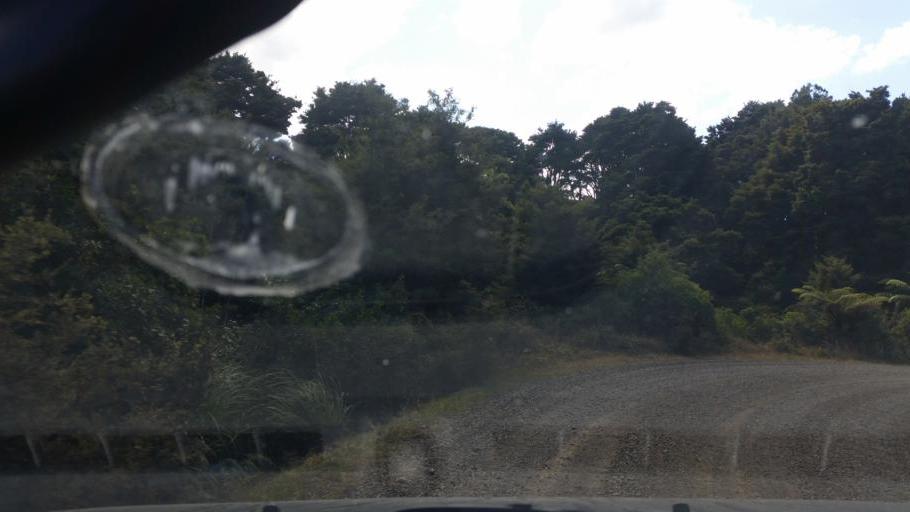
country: NZ
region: Northland
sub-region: Kaipara District
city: Dargaville
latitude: -35.7080
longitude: 173.6072
